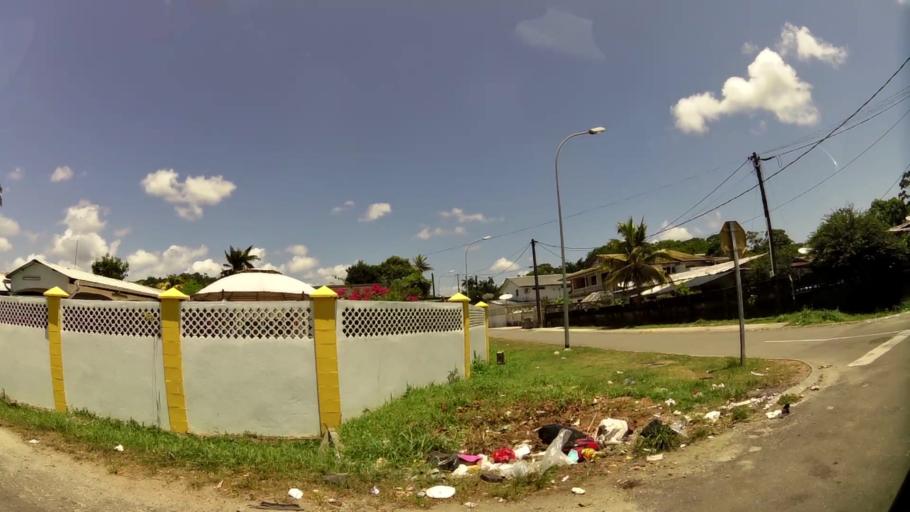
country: GF
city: Macouria
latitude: 4.8883
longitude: -52.3415
